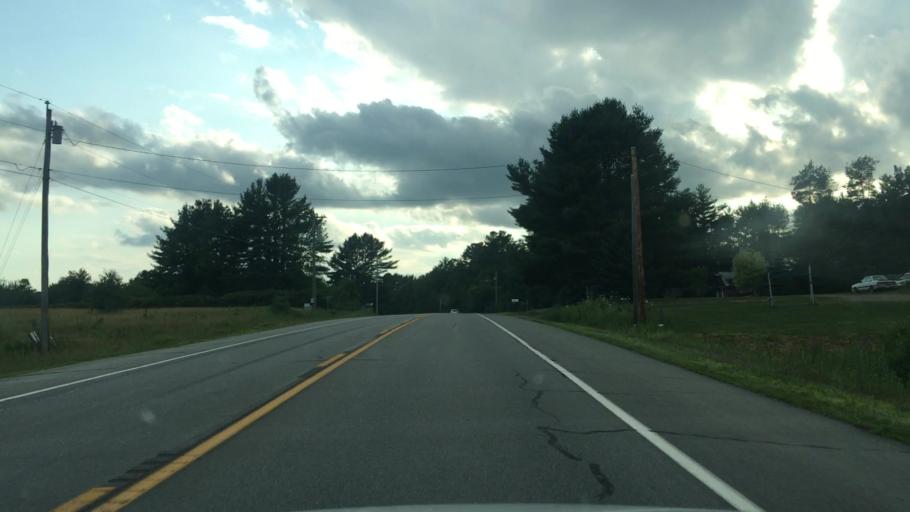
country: US
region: Maine
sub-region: Kennebec County
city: Windsor
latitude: 44.3851
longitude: -69.6102
